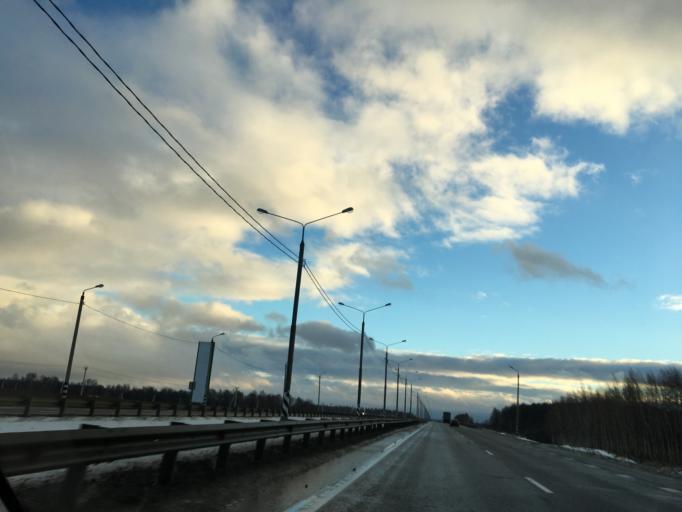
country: RU
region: Tula
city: Zaokskiy
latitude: 54.8036
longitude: 37.4842
